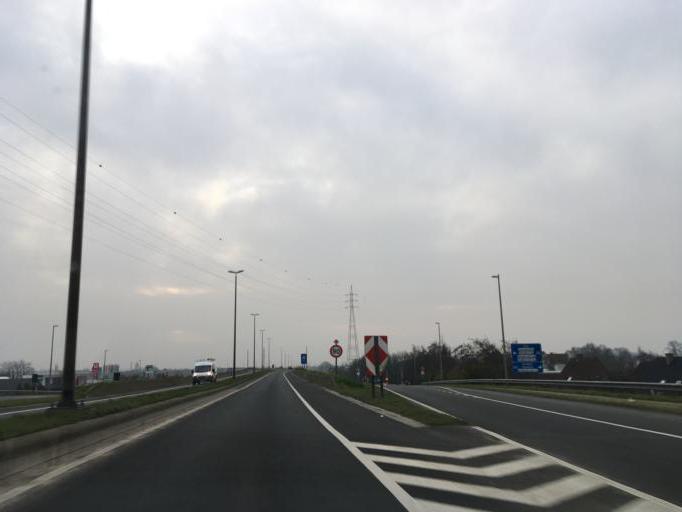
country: BE
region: Flanders
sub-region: Provincie West-Vlaanderen
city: Wielsbeke
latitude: 50.9000
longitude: 3.3962
